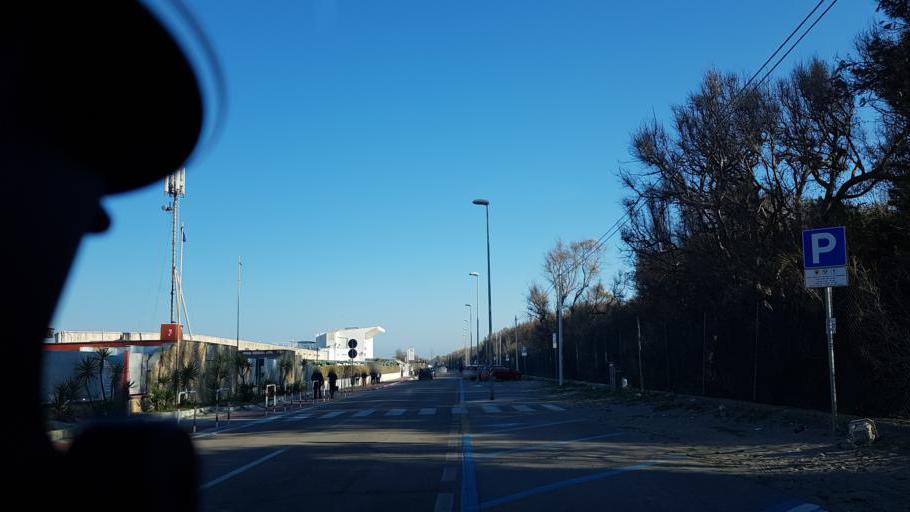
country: IT
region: Apulia
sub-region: Provincia di Lecce
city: Struda
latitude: 40.3829
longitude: 18.3054
